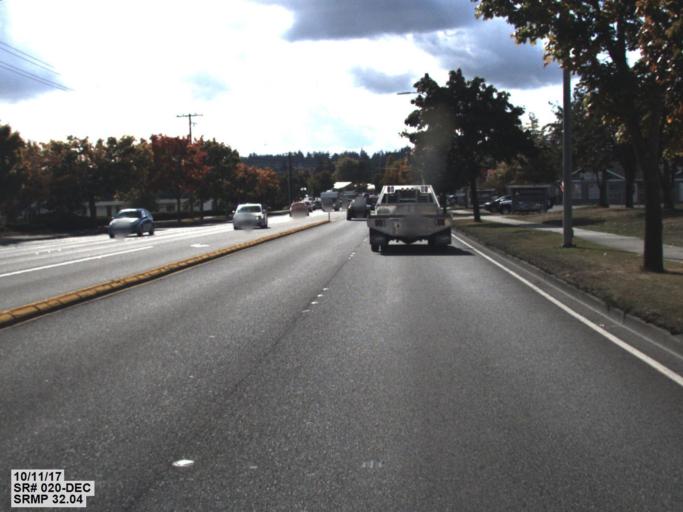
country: US
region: Washington
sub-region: Island County
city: Oak Harbor
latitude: 48.2959
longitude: -122.6552
